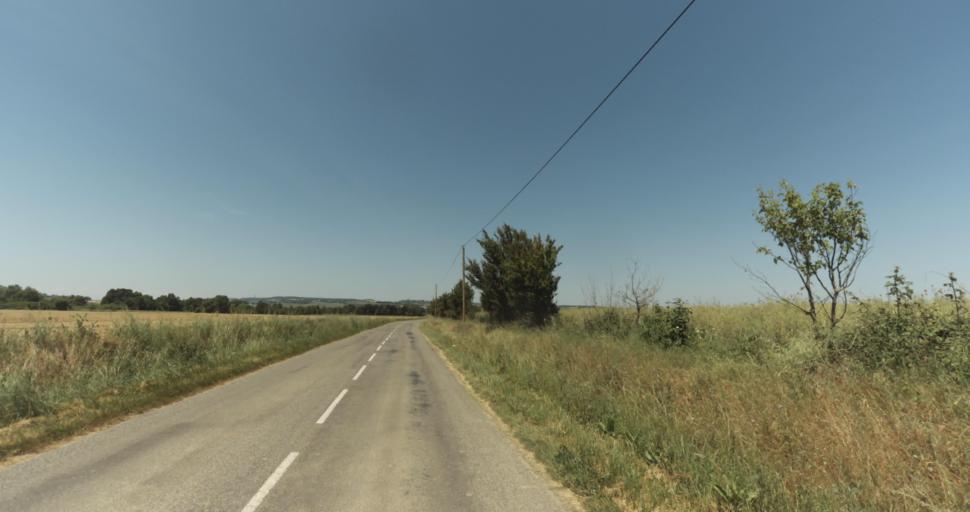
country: FR
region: Midi-Pyrenees
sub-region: Departement du Gers
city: Pujaudran
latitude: 43.6339
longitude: 1.1555
